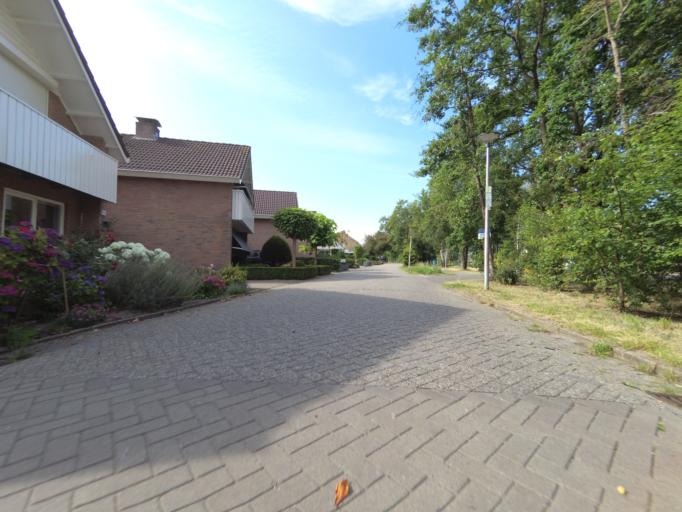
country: NL
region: Overijssel
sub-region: Gemeente Enschede
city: Enschede
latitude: 52.2487
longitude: 6.9106
